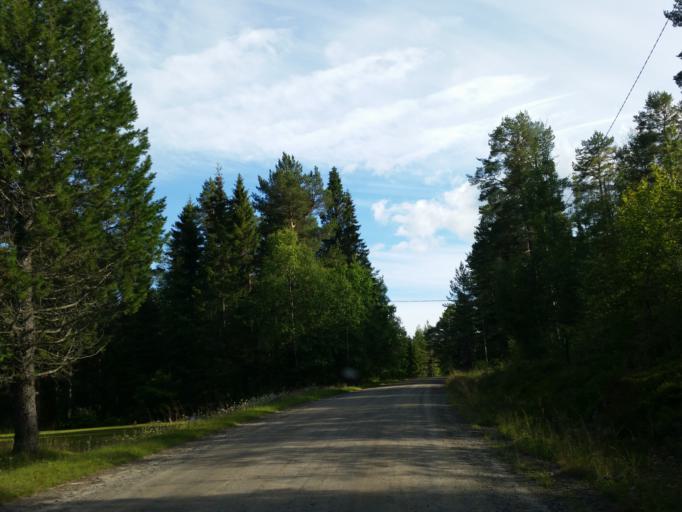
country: SE
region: Vaesterbotten
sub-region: Robertsfors Kommun
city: Robertsfors
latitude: 64.0412
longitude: 20.8500
